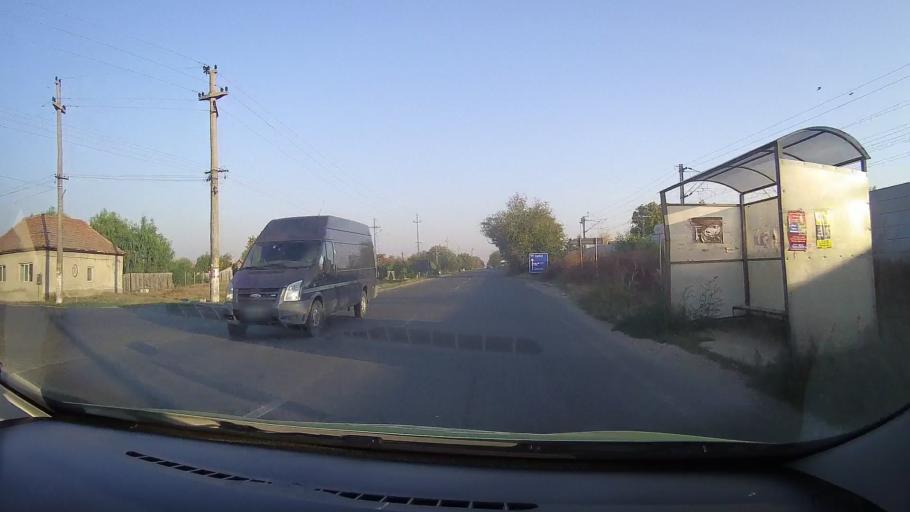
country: RO
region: Arad
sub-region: Comuna Sofronea
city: Sofronea
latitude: 46.2832
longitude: 21.3133
